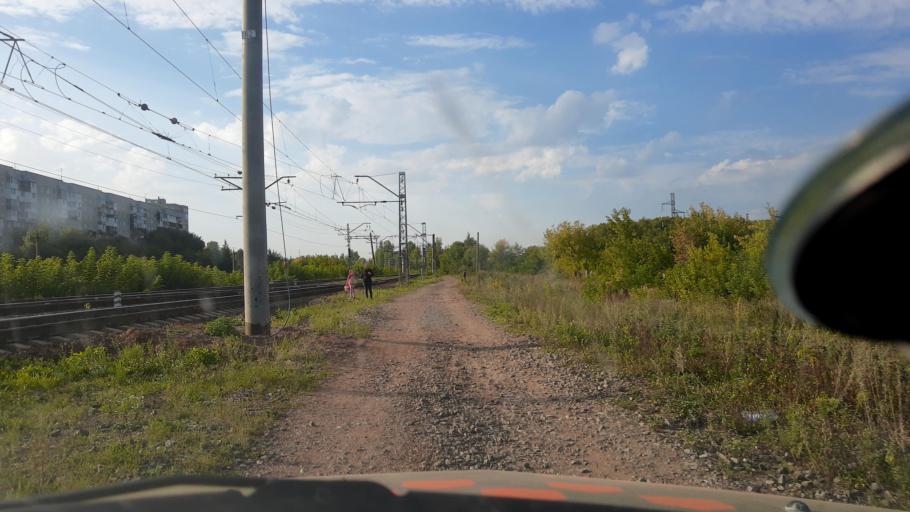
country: RU
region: Bashkortostan
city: Ufa
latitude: 54.8175
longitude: 56.1338
